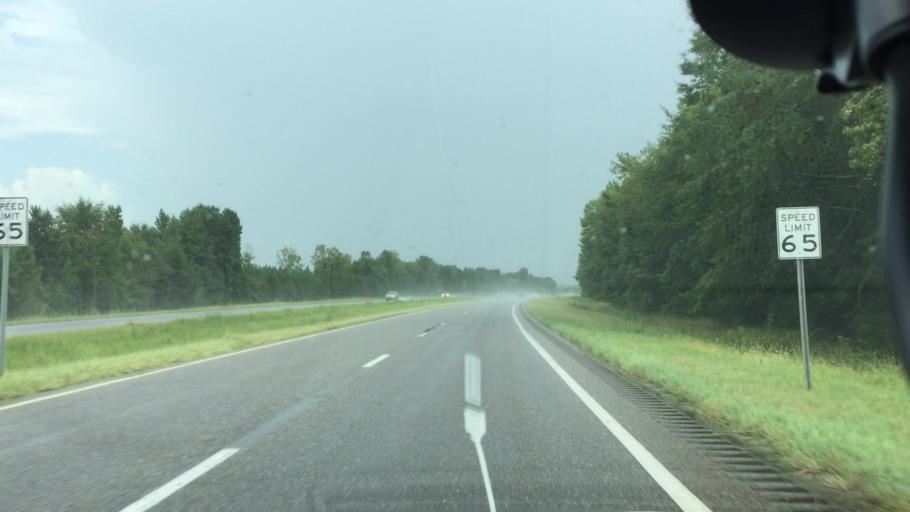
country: US
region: Alabama
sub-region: Montgomery County
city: Pike Road
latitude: 32.2438
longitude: -86.1353
